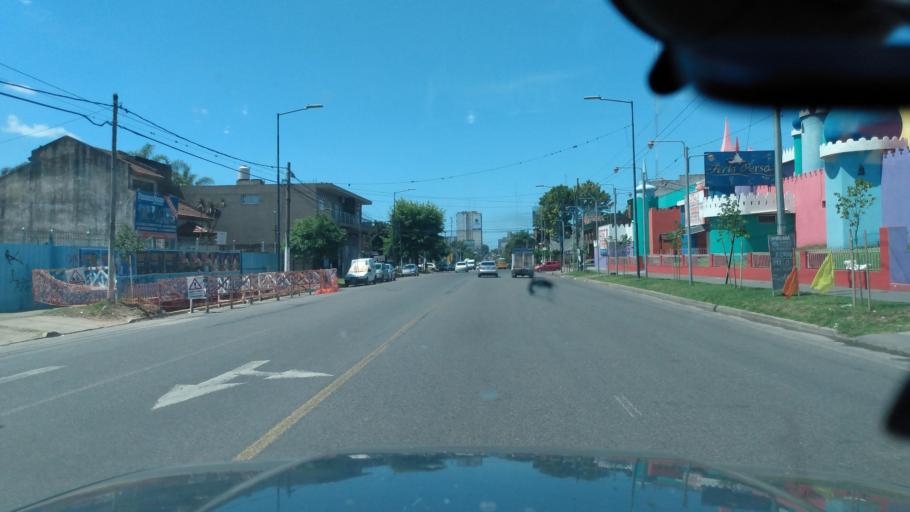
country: AR
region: Buenos Aires
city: Hurlingham
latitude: -34.5498
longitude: -58.7200
